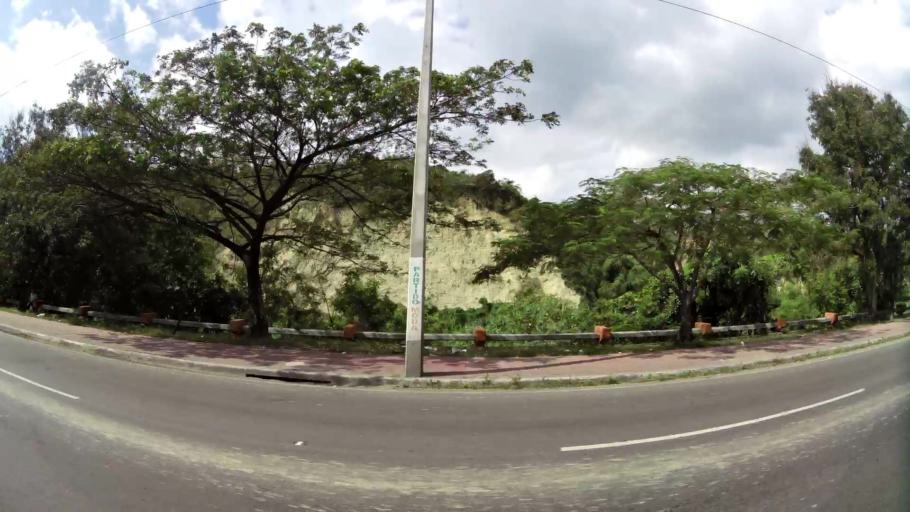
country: DO
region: Santiago
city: Santiago de los Caballeros
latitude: 19.4502
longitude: -70.7138
